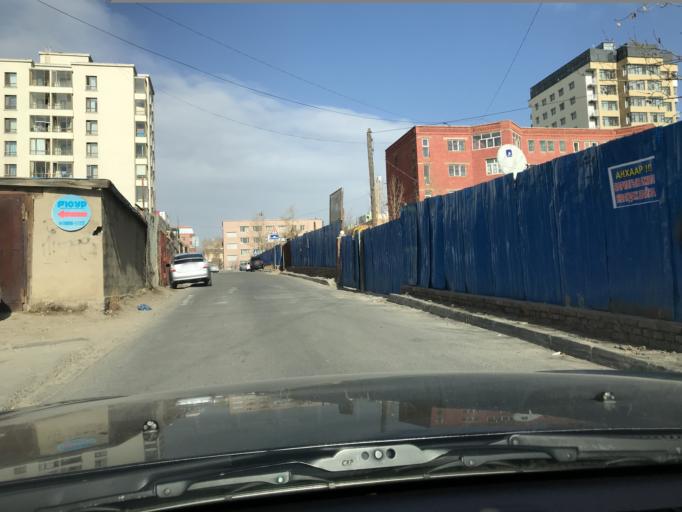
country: MN
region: Ulaanbaatar
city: Ulaanbaatar
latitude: 47.9205
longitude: 106.9400
